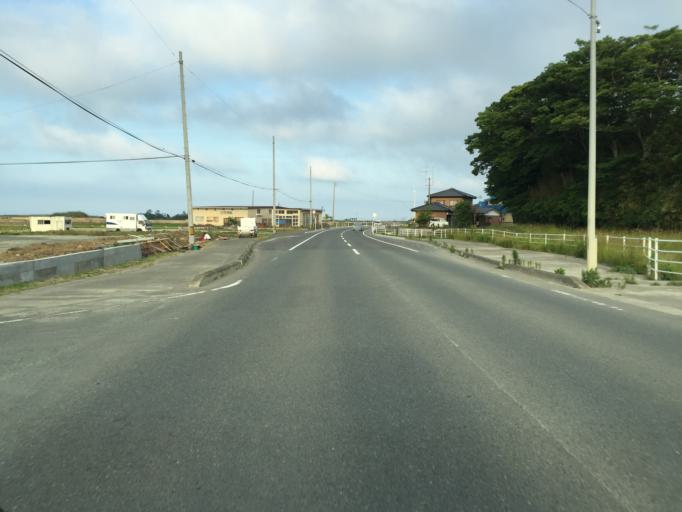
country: JP
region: Miyagi
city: Marumori
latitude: 37.7828
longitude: 140.9650
